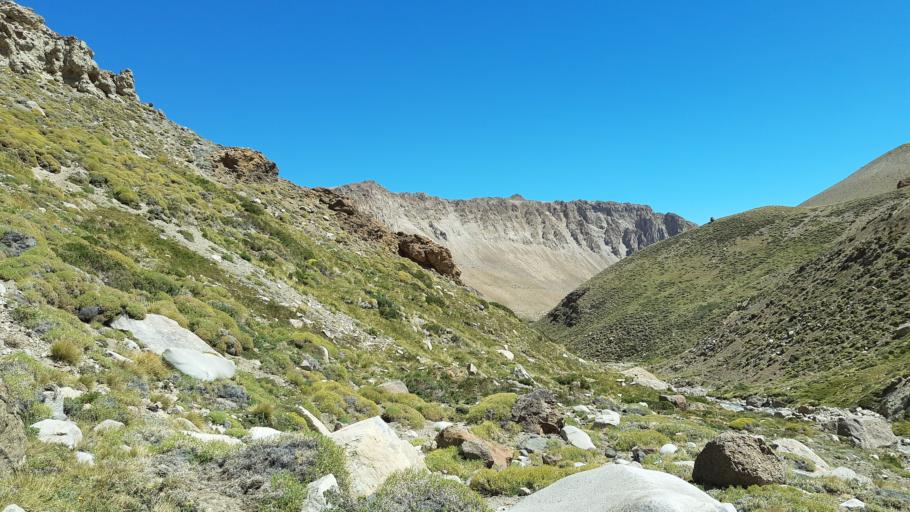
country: AR
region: Neuquen
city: Las Ovejas
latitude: -36.6784
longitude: -70.4931
